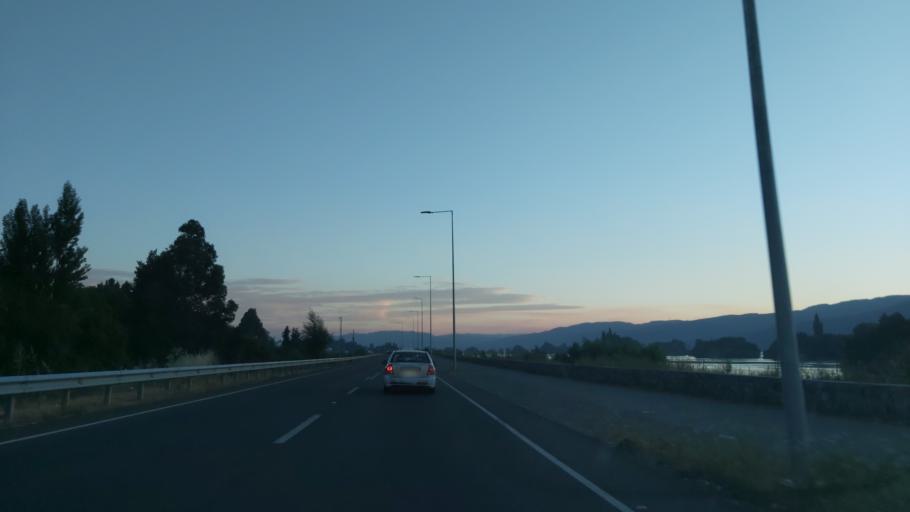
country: CL
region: Biobio
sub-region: Provincia de Concepcion
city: Chiguayante
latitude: -36.8851
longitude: -73.0384
